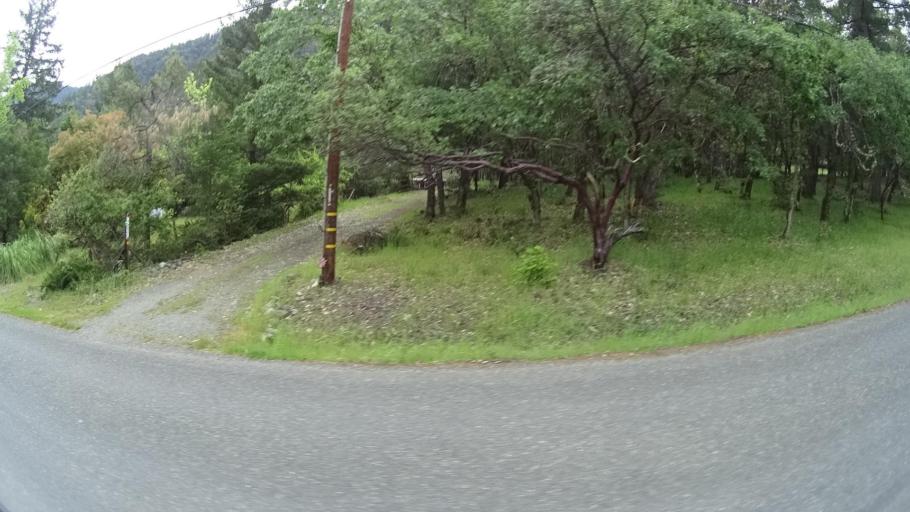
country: US
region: California
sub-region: Humboldt County
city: Willow Creek
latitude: 40.9704
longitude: -123.6305
